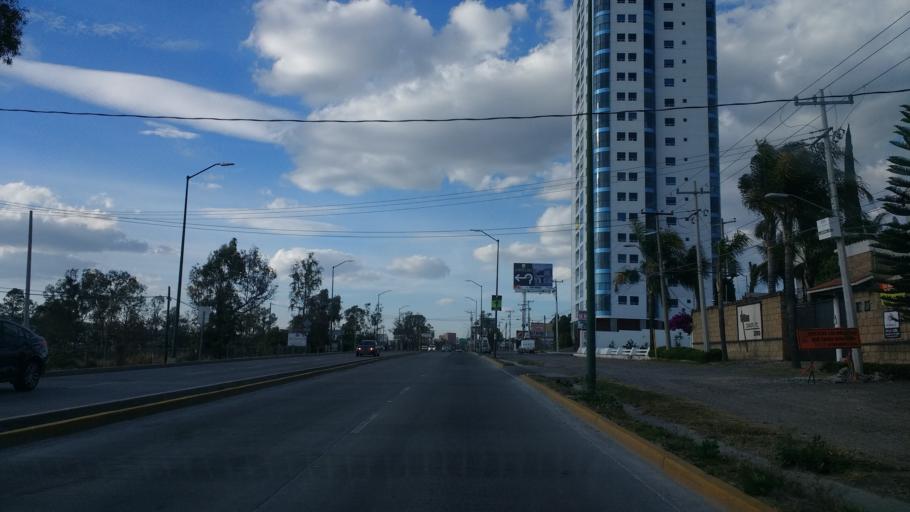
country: MX
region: Guanajuato
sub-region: Leon
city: La Ermita
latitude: 21.1580
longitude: -101.7221
